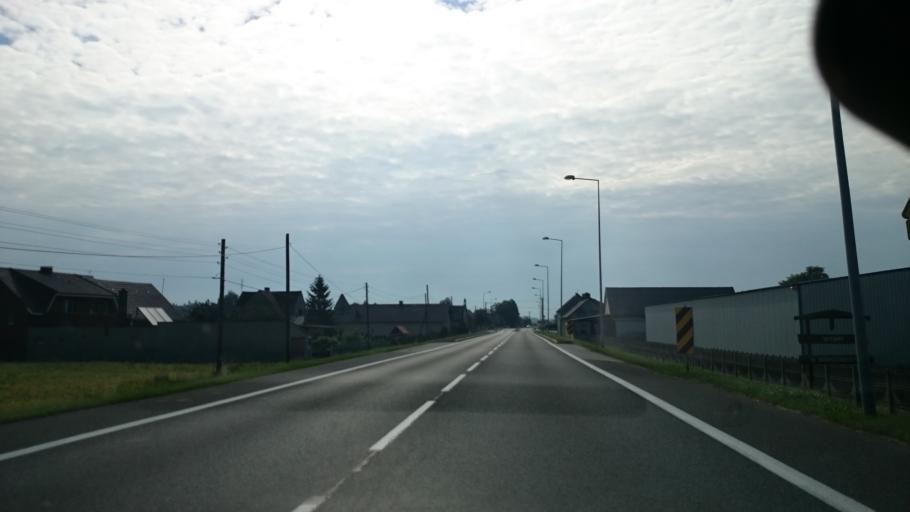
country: PL
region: Opole Voivodeship
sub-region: Powiat strzelecki
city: Jemielnica
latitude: 50.4953
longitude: 18.3727
